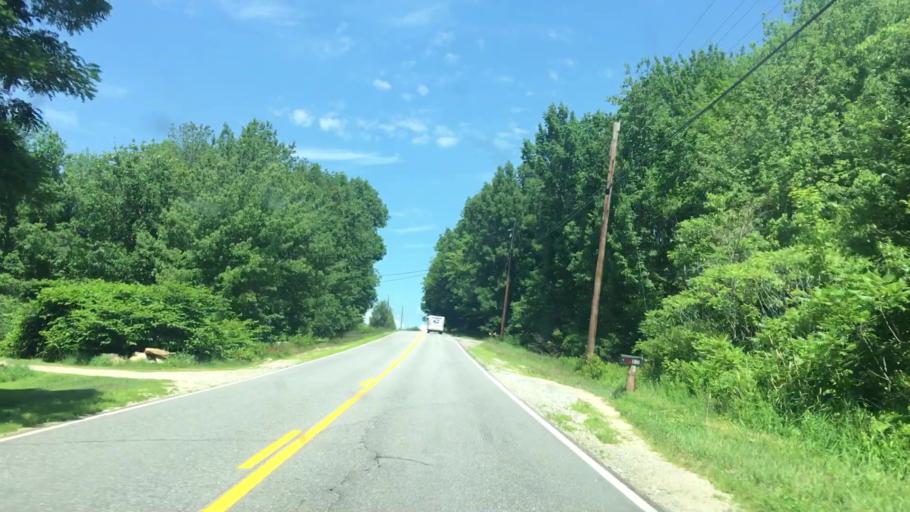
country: US
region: Maine
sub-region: Androscoggin County
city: Livermore
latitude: 44.3670
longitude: -70.2054
